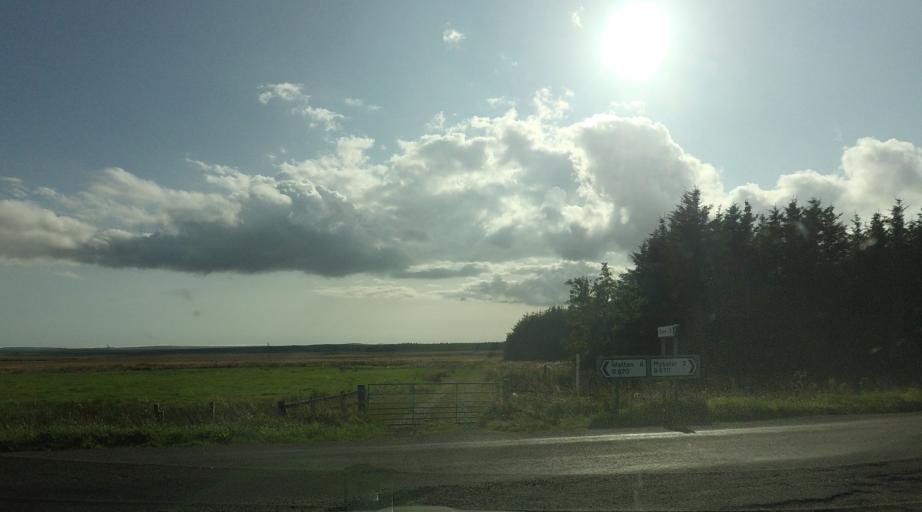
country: GB
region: Scotland
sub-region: Highland
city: Thurso
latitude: 58.4722
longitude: -3.3838
